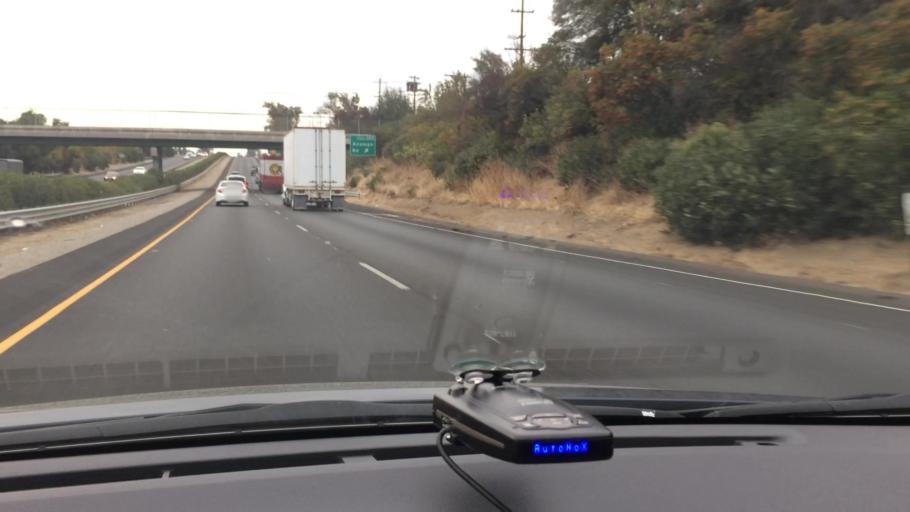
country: US
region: California
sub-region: San Joaquin County
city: Collierville
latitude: 38.1737
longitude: -121.2622
